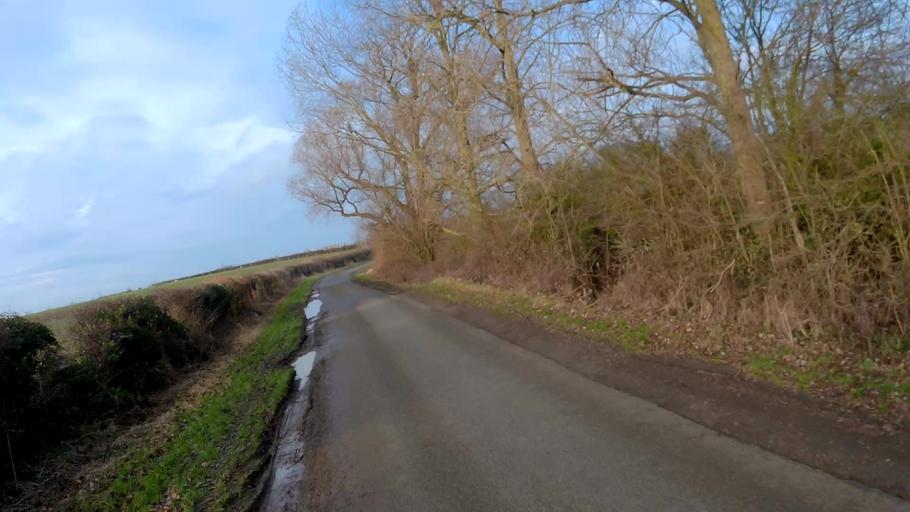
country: GB
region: England
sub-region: Lincolnshire
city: Bourne
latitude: 52.7723
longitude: -0.4253
